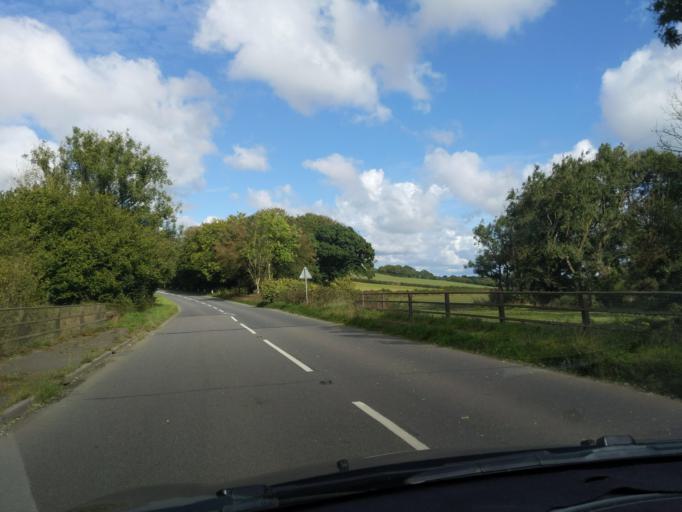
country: GB
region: England
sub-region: Devon
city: Holsworthy
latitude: 50.8701
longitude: -4.3201
